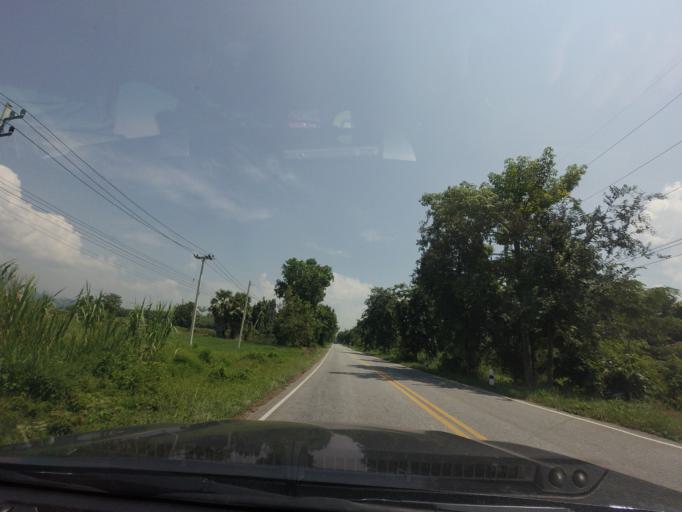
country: TH
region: Uttaradit
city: Thong Saen Khan
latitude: 17.4618
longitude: 100.2915
